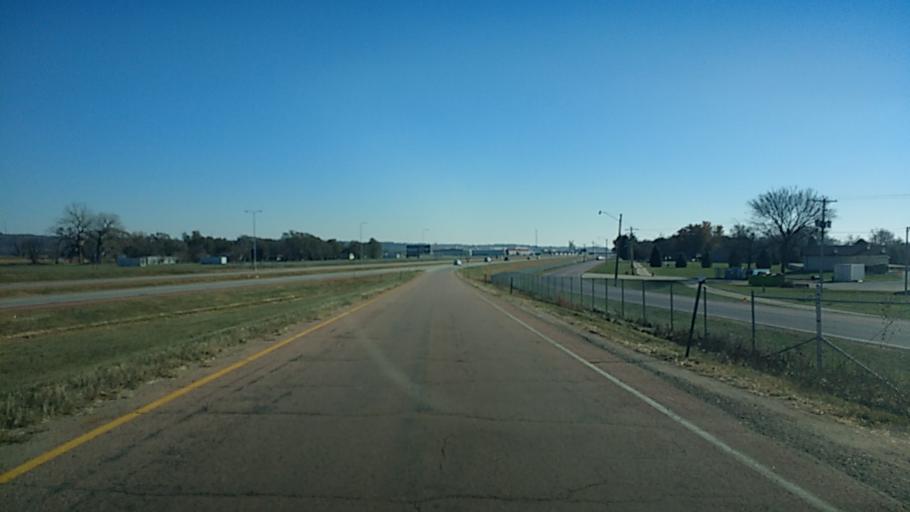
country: US
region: South Dakota
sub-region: Union County
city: North Sioux City
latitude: 42.5495
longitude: -96.5093
